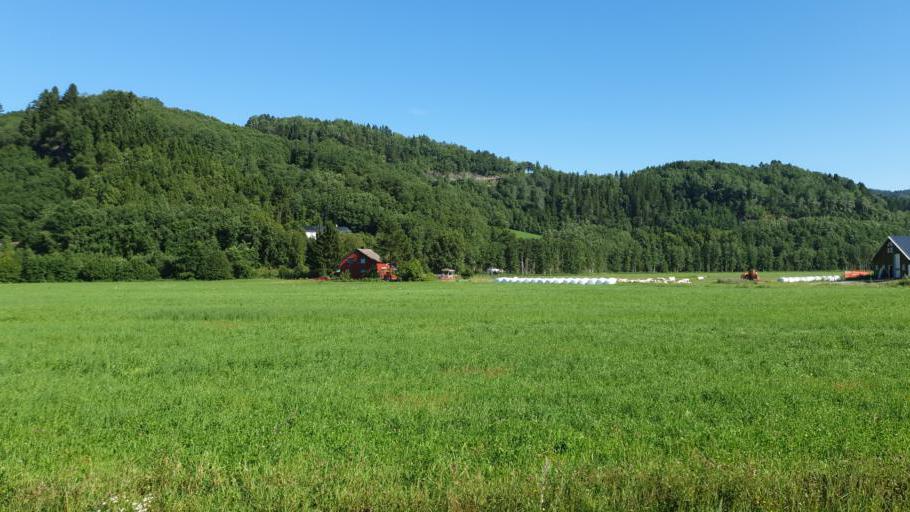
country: NO
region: Sor-Trondelag
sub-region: Orkdal
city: Orkanger
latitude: 63.2081
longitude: 9.7863
